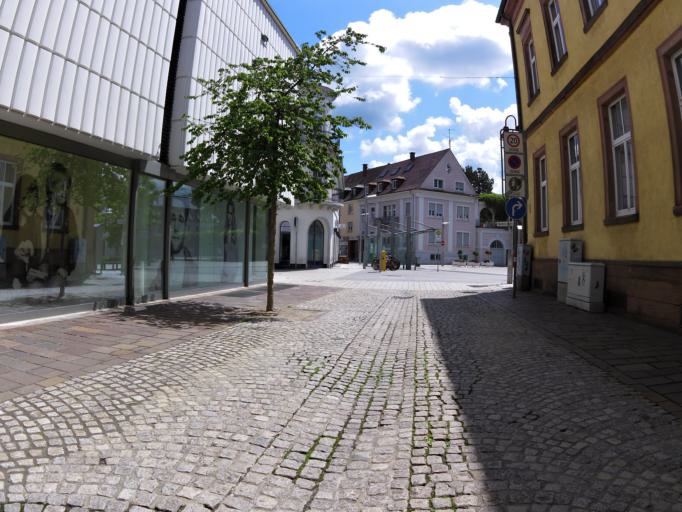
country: DE
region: Baden-Wuerttemberg
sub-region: Freiburg Region
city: Lahr
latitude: 48.3386
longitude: 7.8714
